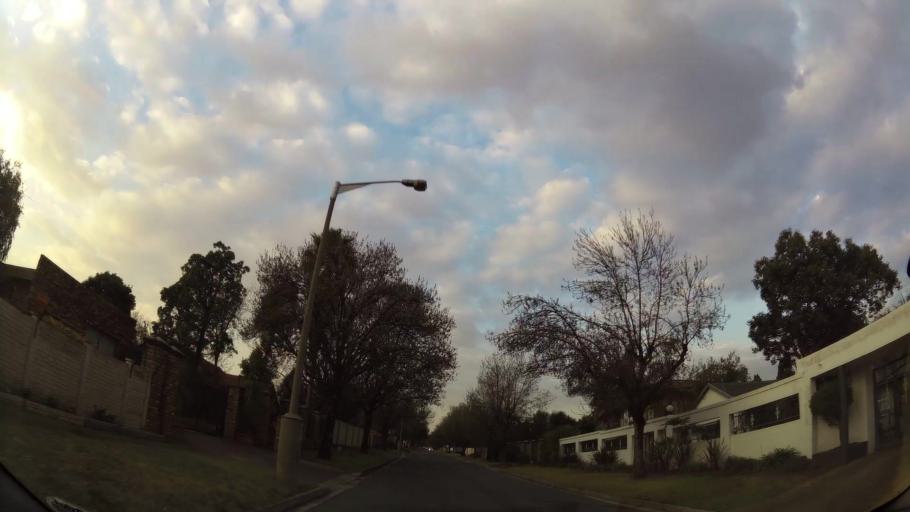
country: ZA
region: Gauteng
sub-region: Ekurhuleni Metropolitan Municipality
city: Benoni
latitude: -26.1735
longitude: 28.2966
